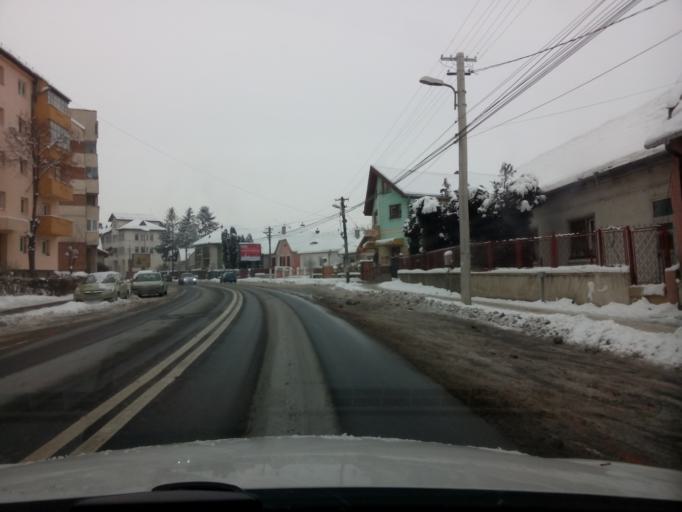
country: RO
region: Sibiu
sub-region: Municipiul Sibiu
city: Sibiu
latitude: 45.8078
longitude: 24.1515
